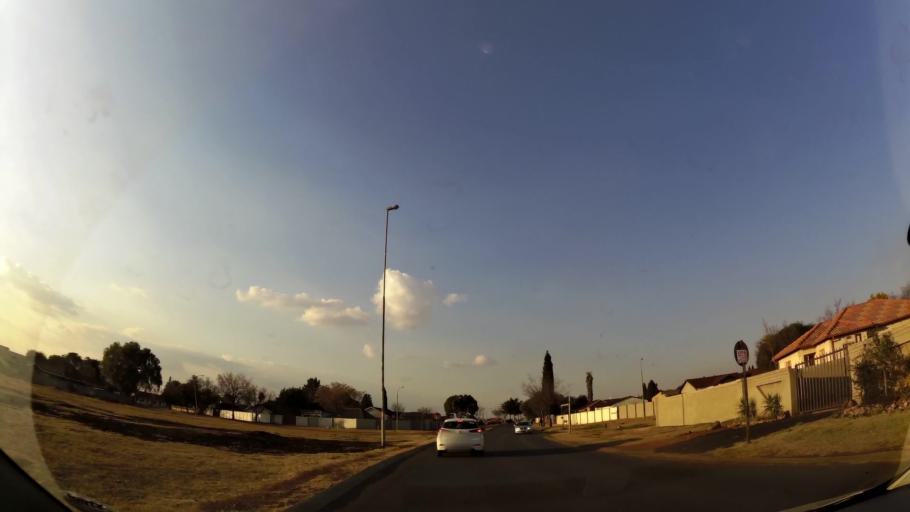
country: ZA
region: Gauteng
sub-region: Ekurhuleni Metropolitan Municipality
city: Boksburg
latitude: -26.2978
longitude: 28.2492
